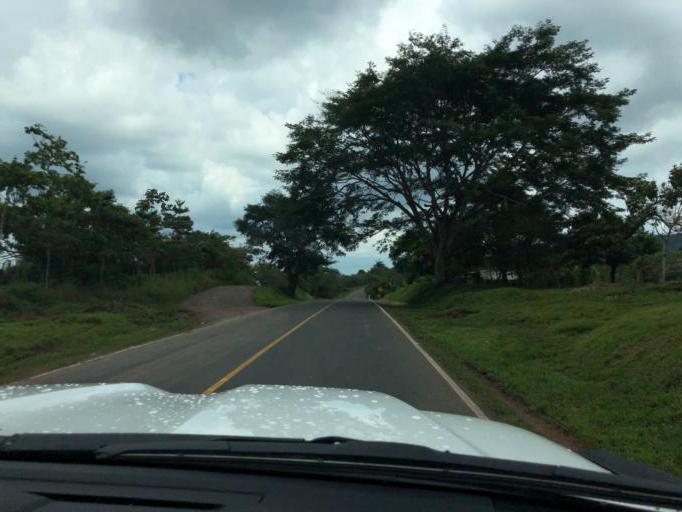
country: NI
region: Chontales
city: Villa Sandino
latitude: 11.9946
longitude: -84.8571
